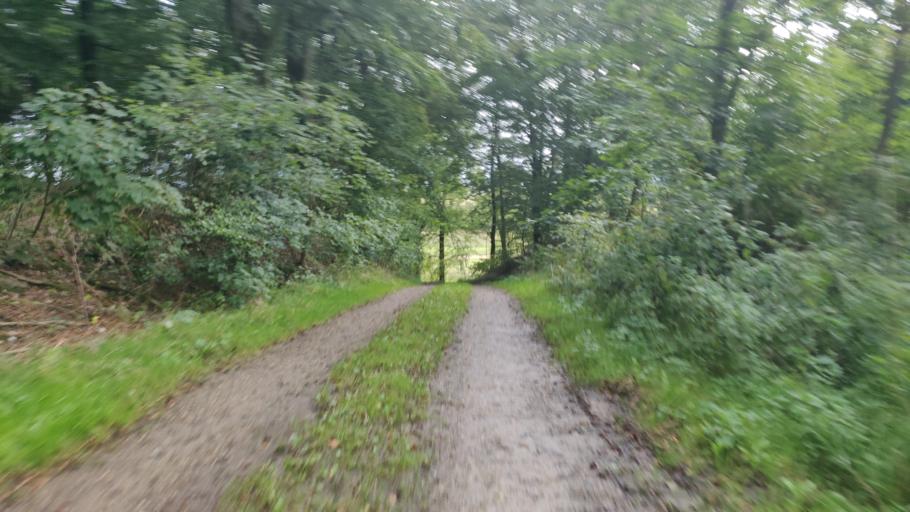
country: DK
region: South Denmark
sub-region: Kolding Kommune
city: Lunderskov
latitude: 55.5423
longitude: 9.3651
